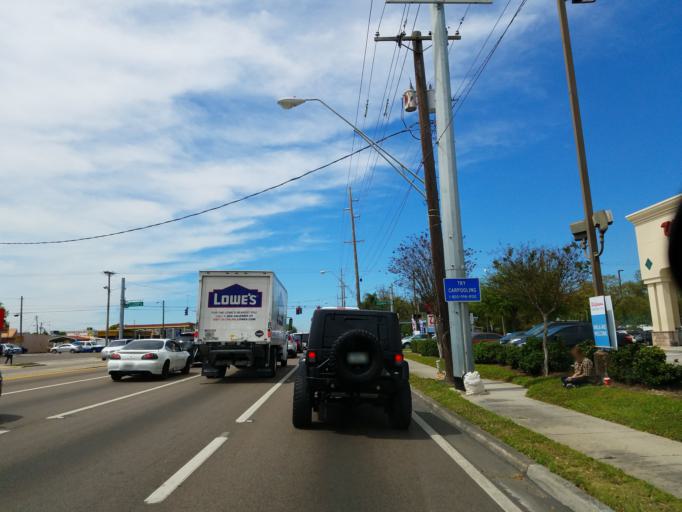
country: US
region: Florida
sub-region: Hillsborough County
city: Brandon
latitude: 27.9378
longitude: -82.2848
